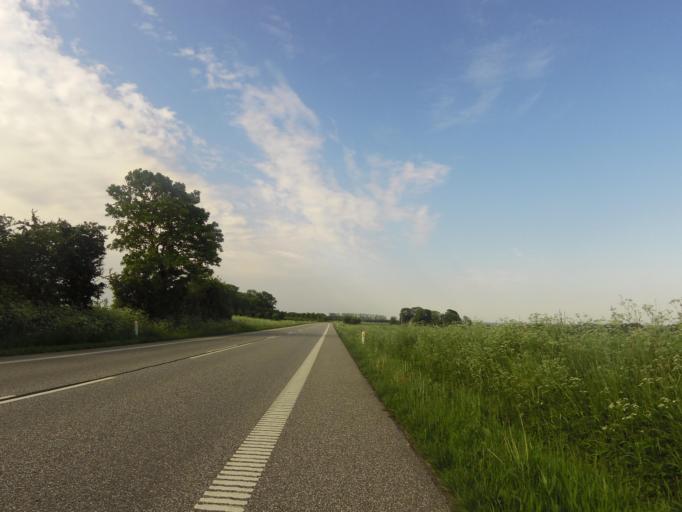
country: DK
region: South Denmark
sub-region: Haderslev Kommune
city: Gram
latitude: 55.2789
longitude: 9.0291
